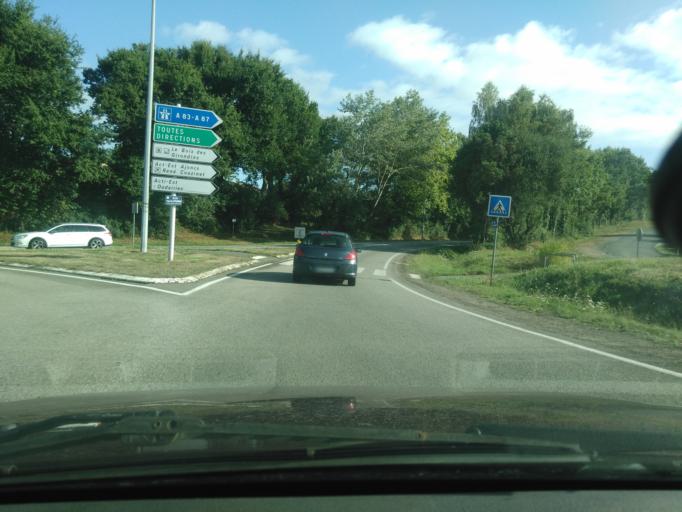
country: FR
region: Pays de la Loire
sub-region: Departement de la Vendee
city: La Roche-sur-Yon
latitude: 46.6697
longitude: -1.4095
